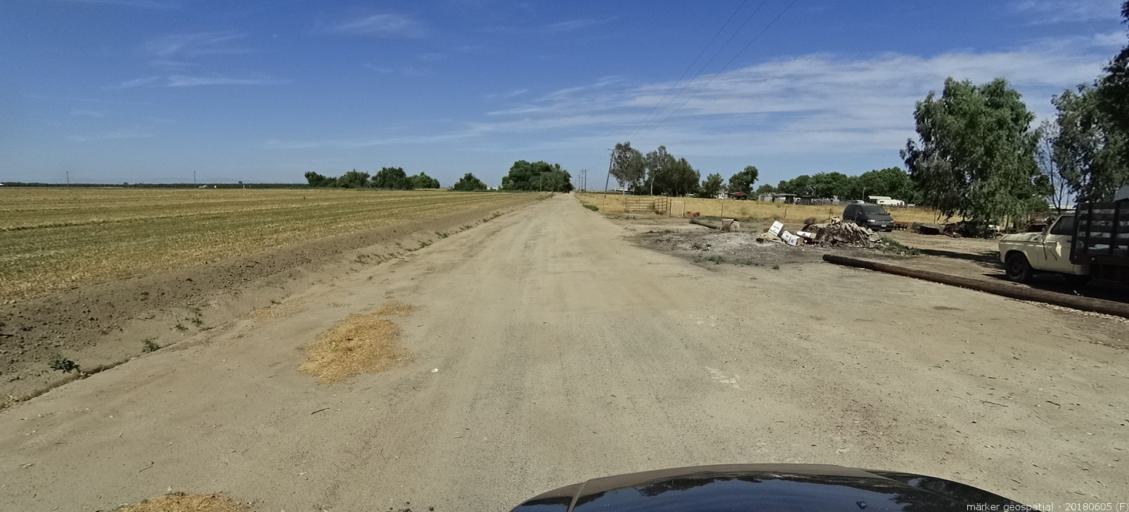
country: US
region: California
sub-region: Madera County
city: Chowchilla
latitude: 37.1199
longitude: -120.3907
